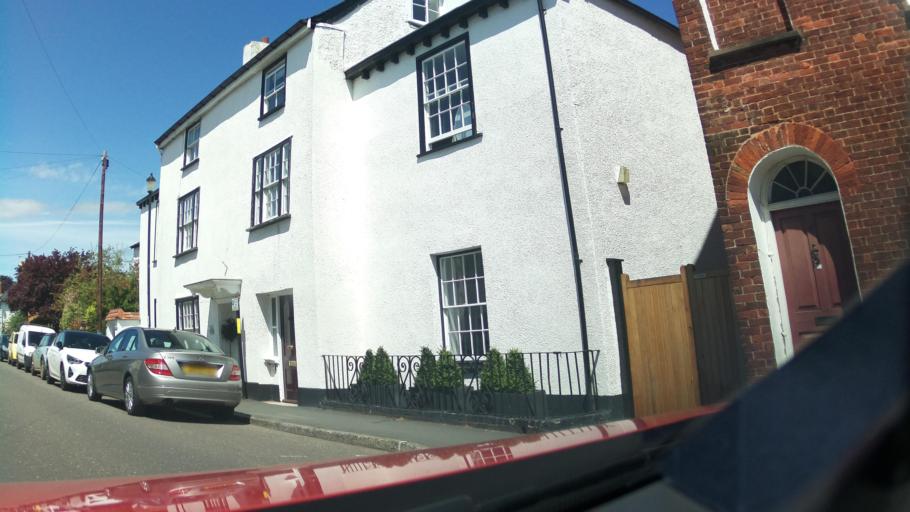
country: GB
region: England
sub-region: Devon
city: Topsham
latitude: 50.6865
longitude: -3.4676
